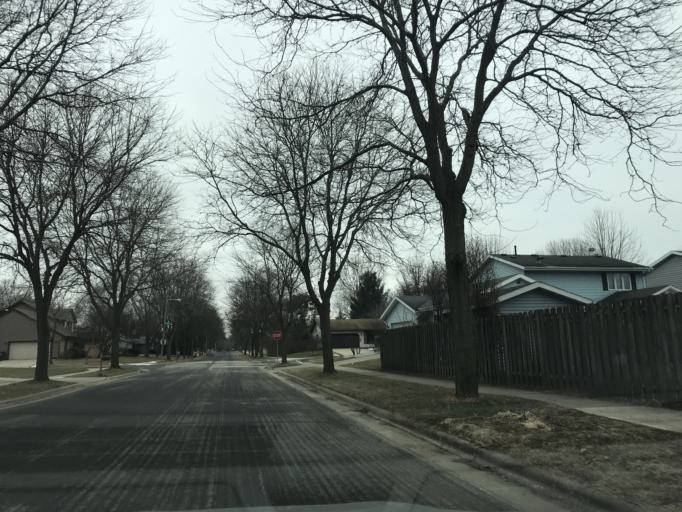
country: US
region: Wisconsin
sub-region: Dane County
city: Monona
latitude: 43.0969
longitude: -89.2921
